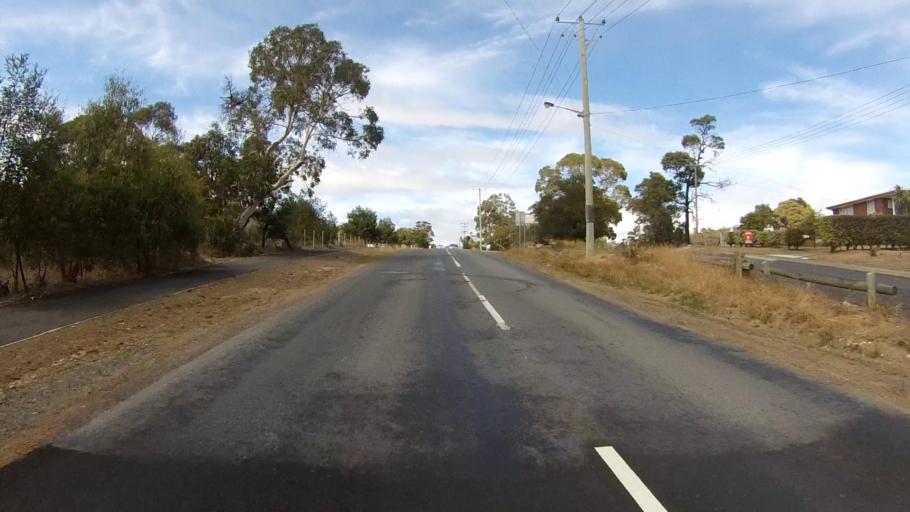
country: AU
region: Tasmania
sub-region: Clarence
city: Lindisfarne
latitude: -42.8154
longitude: 147.3514
